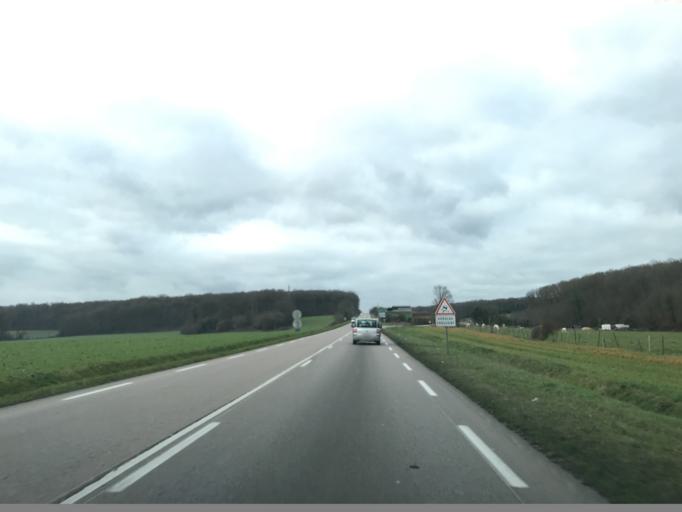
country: FR
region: Haute-Normandie
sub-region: Departement de l'Eure
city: Fleury-sur-Andelle
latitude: 49.3665
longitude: 1.3471
